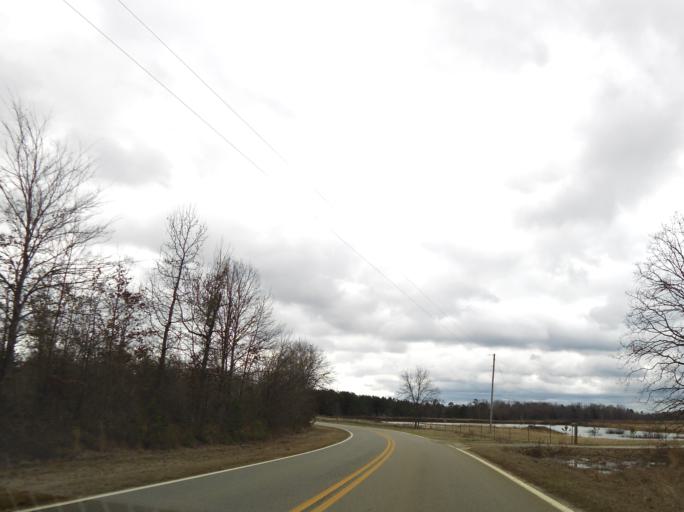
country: US
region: Georgia
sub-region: Bleckley County
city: Cochran
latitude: 32.5374
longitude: -83.3730
